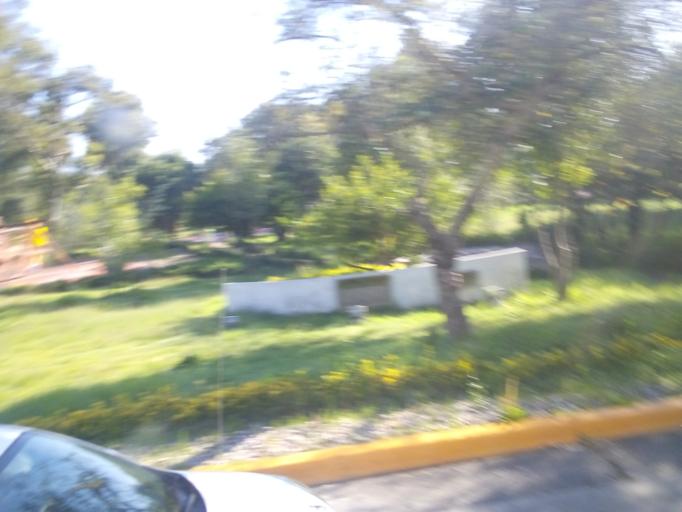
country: MX
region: Mexico
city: Vista Hermosa
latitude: 19.5143
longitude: -99.2375
